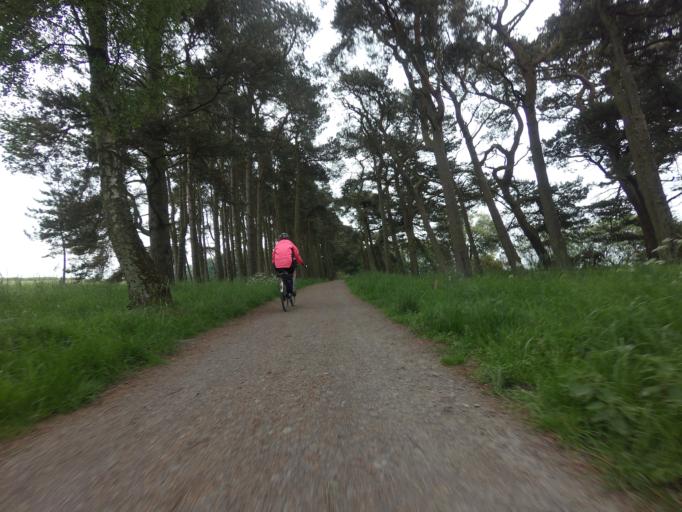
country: GB
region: Scotland
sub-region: Perth and Kinross
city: Milnathort
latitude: 56.2201
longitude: -3.3924
